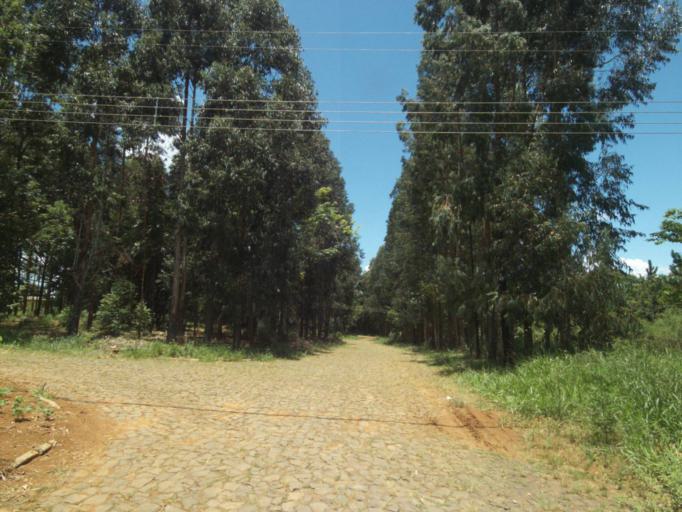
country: BR
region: Parana
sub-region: Pinhao
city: Pinhao
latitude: -25.7887
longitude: -52.0875
